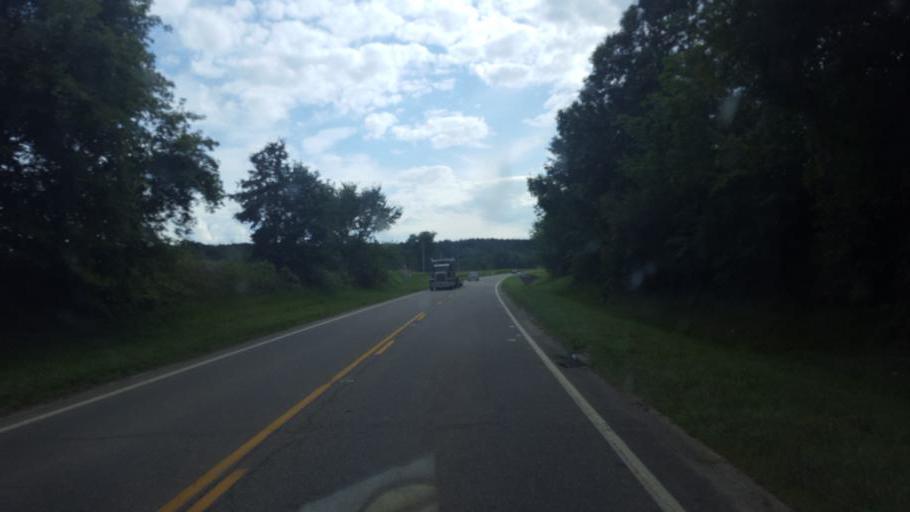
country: US
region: Ohio
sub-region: Tuscarawas County
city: Dover
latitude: 40.6277
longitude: -81.3592
